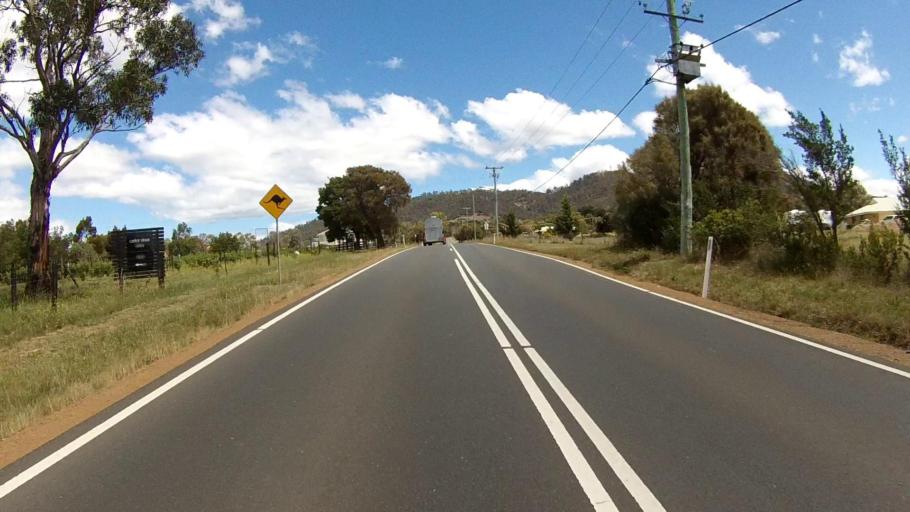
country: AU
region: Tasmania
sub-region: Clarence
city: Seven Mile Beach
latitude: -42.8480
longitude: 147.4781
